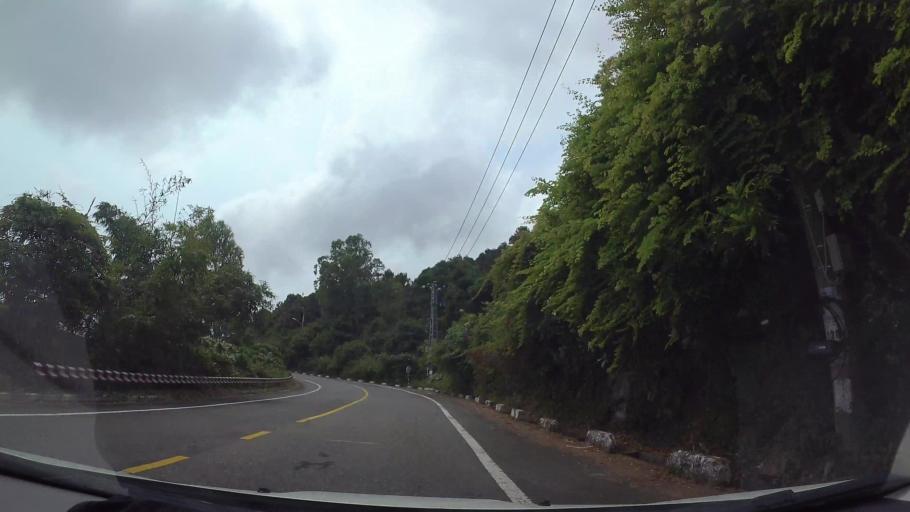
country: VN
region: Da Nang
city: Son Tra
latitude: 16.1065
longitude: 108.2978
